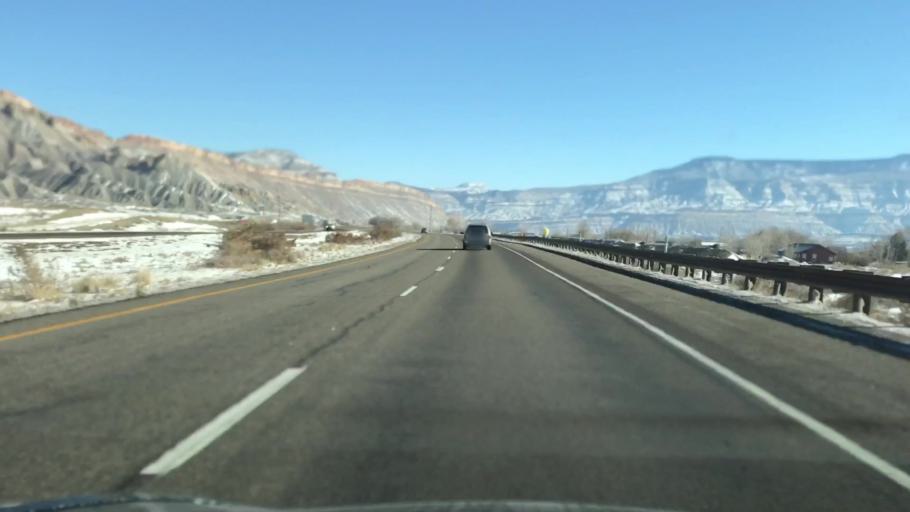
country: US
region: Colorado
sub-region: Mesa County
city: Clifton
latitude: 39.1075
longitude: -108.4308
